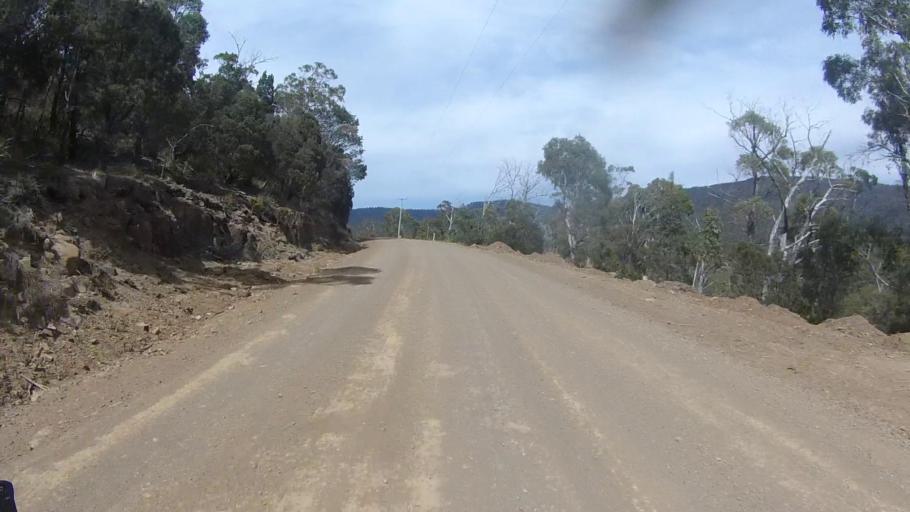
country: AU
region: Tasmania
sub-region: Sorell
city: Sorell
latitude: -42.6684
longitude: 147.8857
